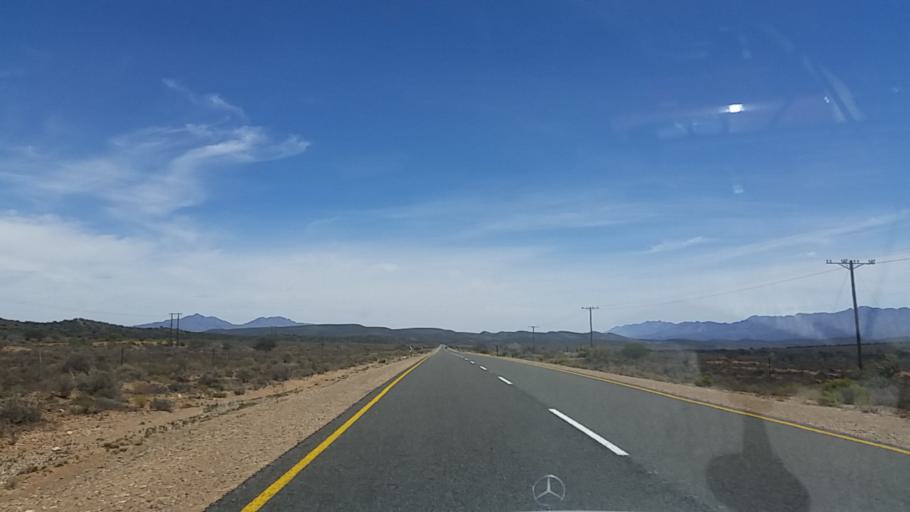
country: ZA
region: Eastern Cape
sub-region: Cacadu District Municipality
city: Willowmore
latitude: -33.5019
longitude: 23.2510
